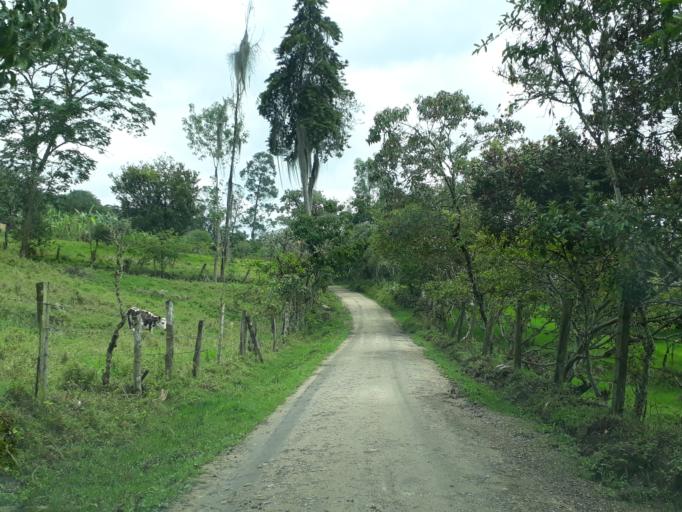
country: CO
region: Cundinamarca
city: Manta
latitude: 4.9812
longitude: -73.5603
